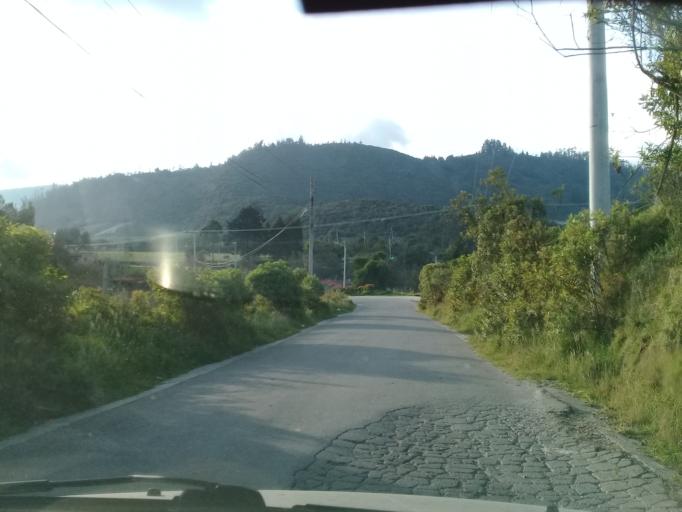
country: CO
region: Cundinamarca
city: Sibate
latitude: 4.4662
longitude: -74.2646
